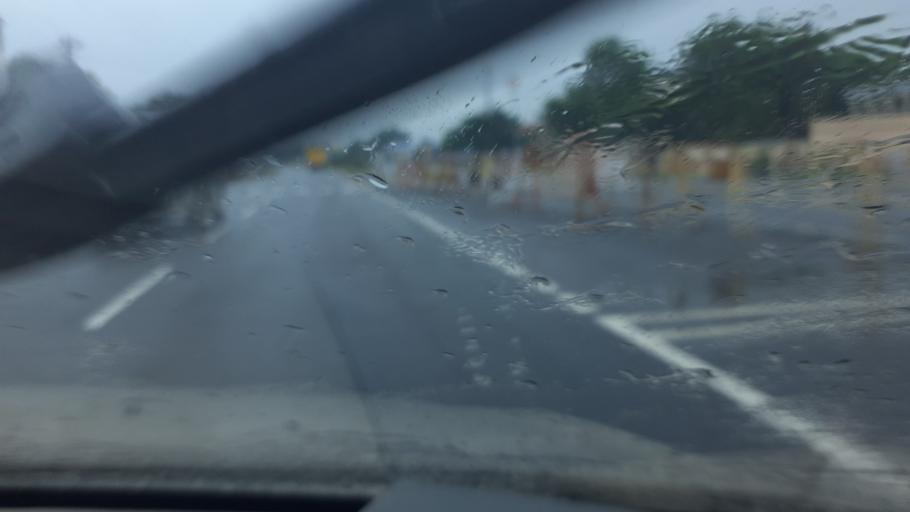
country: IN
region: Tamil Nadu
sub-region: Virudhunagar
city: Virudunagar
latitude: 9.6091
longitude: 77.9562
